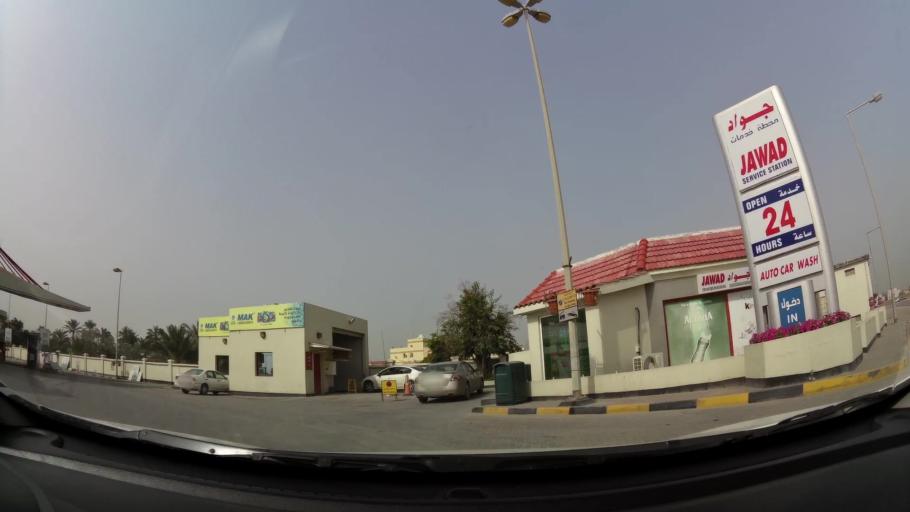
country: BH
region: Manama
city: Jidd Hafs
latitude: 26.2248
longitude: 50.5212
